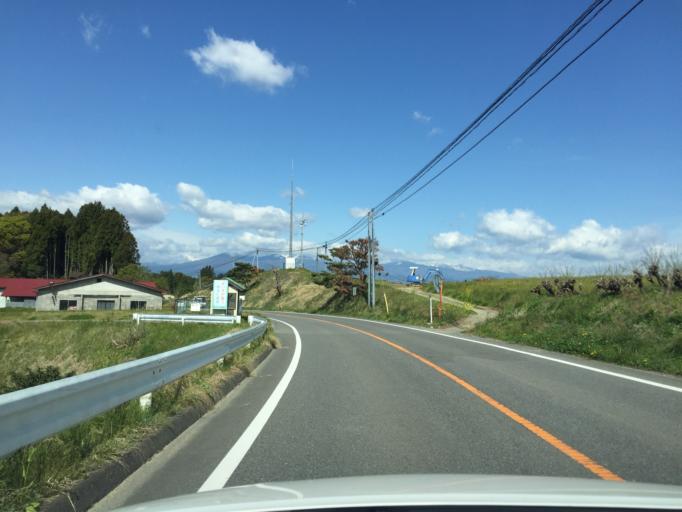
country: JP
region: Fukushima
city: Funehikimachi-funehiki
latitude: 37.5400
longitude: 140.5759
